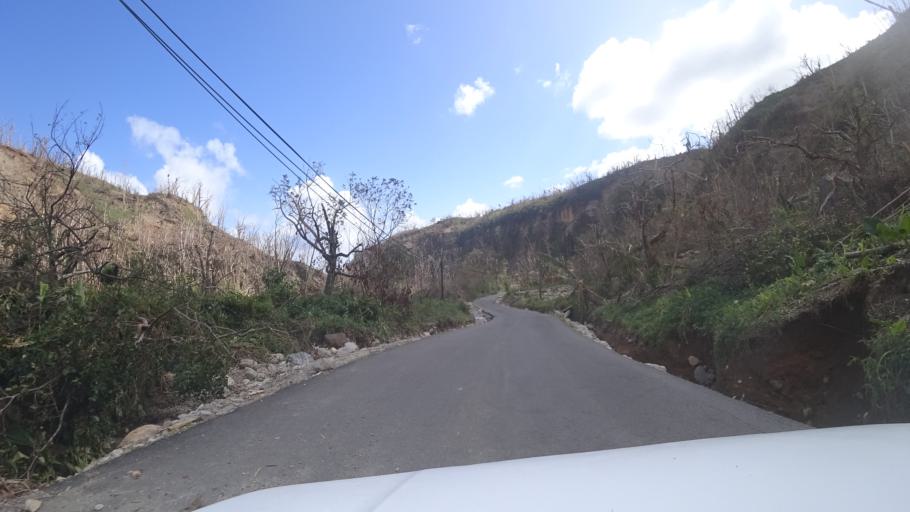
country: DM
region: Saint Patrick
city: Berekua
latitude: 15.2594
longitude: -61.3183
